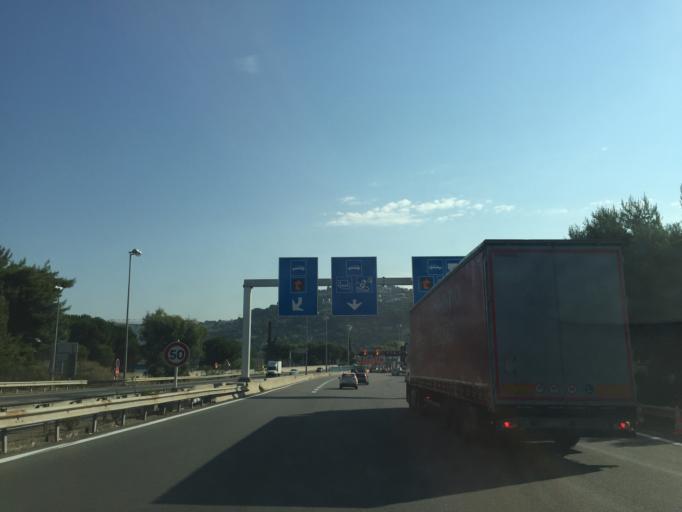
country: FR
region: Provence-Alpes-Cote d'Azur
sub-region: Departement des Alpes-Maritimes
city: Saint-Laurent-du-Var
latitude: 43.7062
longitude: 7.1895
